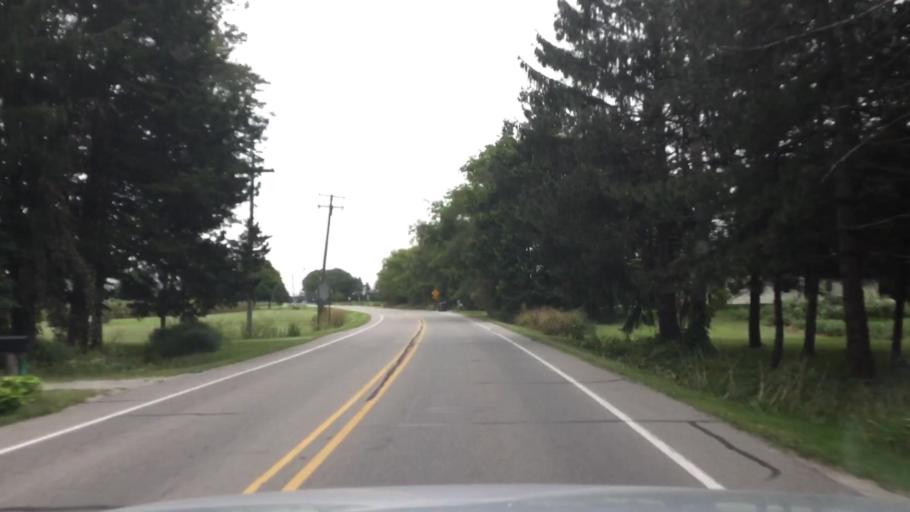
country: US
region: Michigan
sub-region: Washtenaw County
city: Milan
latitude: 42.1115
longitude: -83.7216
